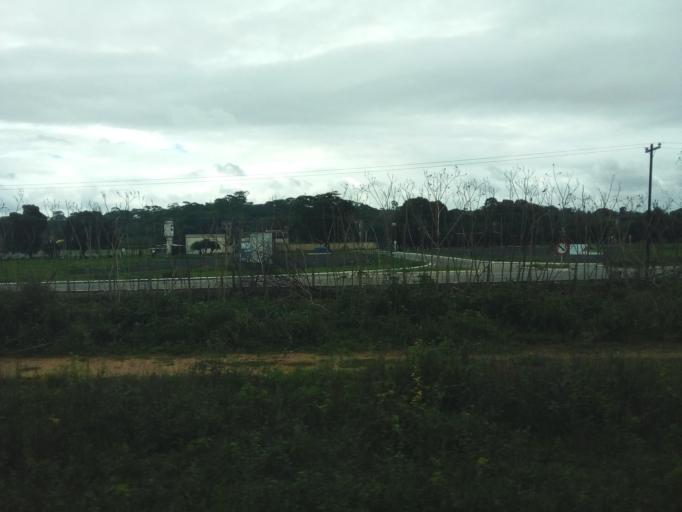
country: BR
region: Minas Gerais
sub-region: Ipatinga
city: Ipatinga
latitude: -19.4760
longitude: -42.4865
